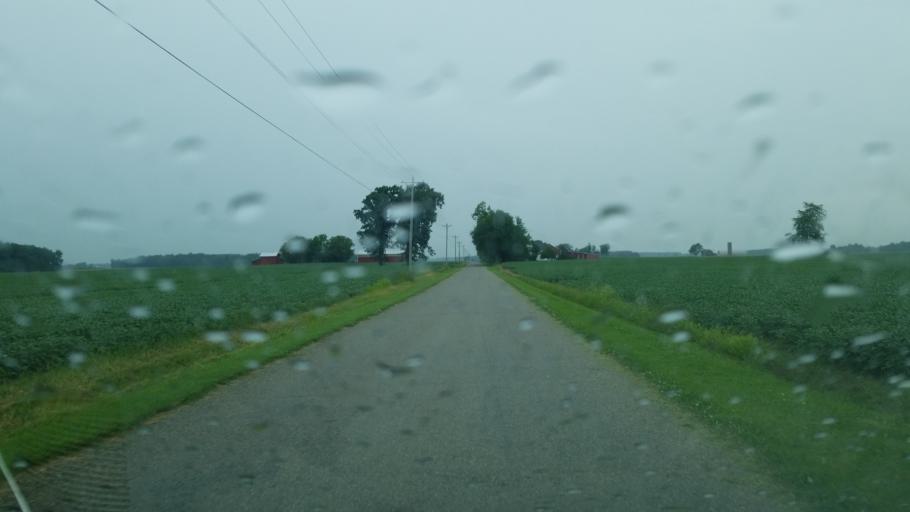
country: US
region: Ohio
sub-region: Huron County
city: Willard
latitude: 41.0017
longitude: -82.8137
